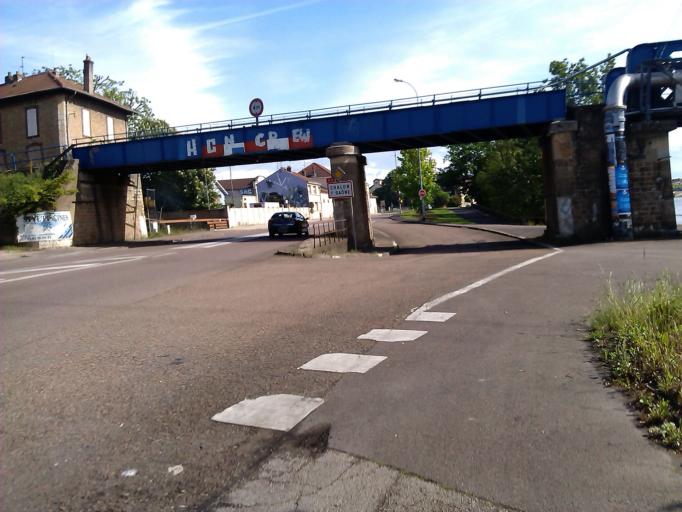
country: FR
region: Bourgogne
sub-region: Departement de Saone-et-Loire
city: Chalon-sur-Saone
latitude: 46.7737
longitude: 4.8448
